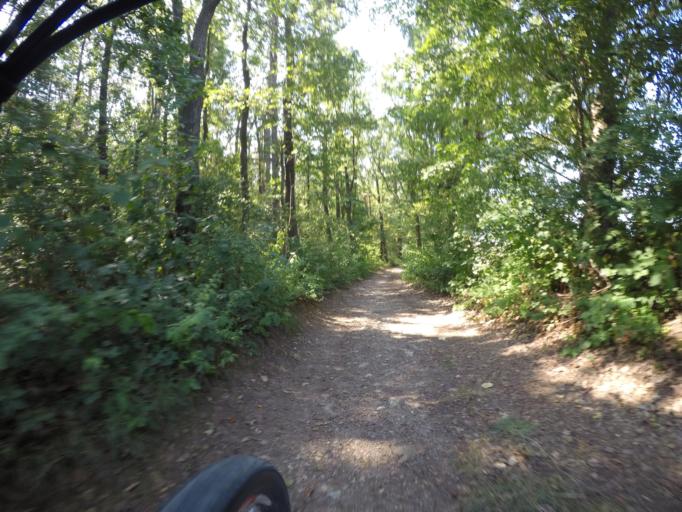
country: AT
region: Lower Austria
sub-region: Politischer Bezirk Baden
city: Hirtenberg
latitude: 47.9465
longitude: 16.1690
